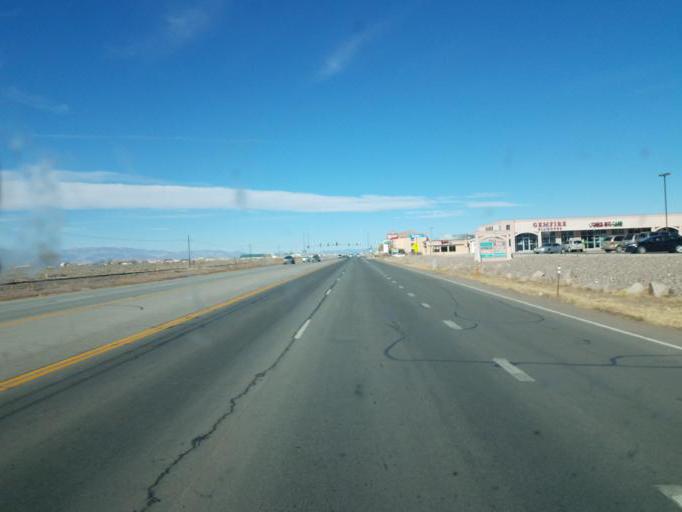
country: US
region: Colorado
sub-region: Alamosa County
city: Alamosa
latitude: 37.4792
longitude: -105.9039
